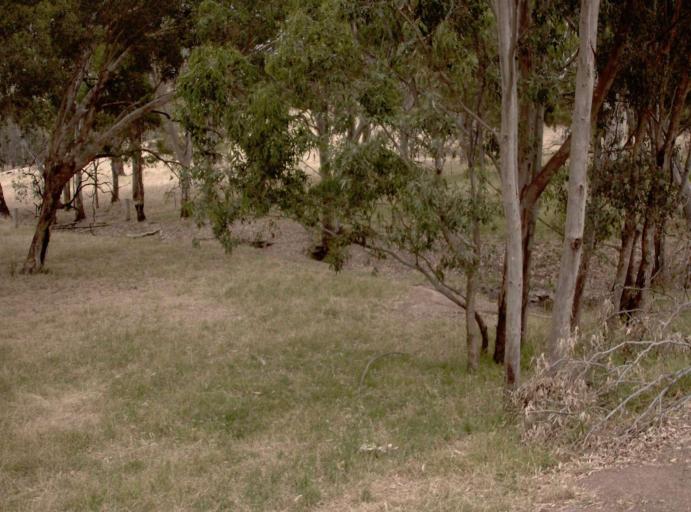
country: AU
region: Victoria
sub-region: Wellington
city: Heyfield
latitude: -37.6599
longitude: 146.6461
